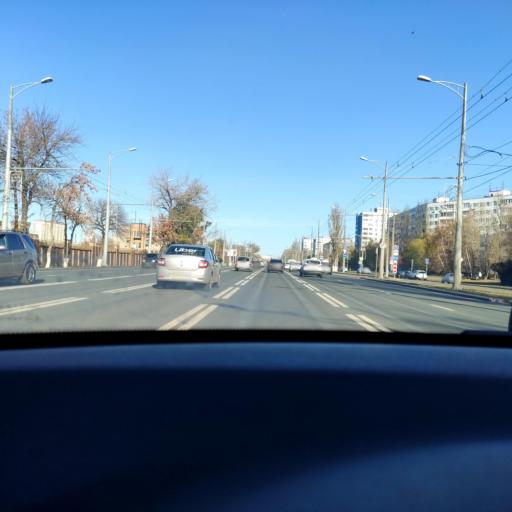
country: RU
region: Samara
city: Samara
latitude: 53.2355
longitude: 50.2006
